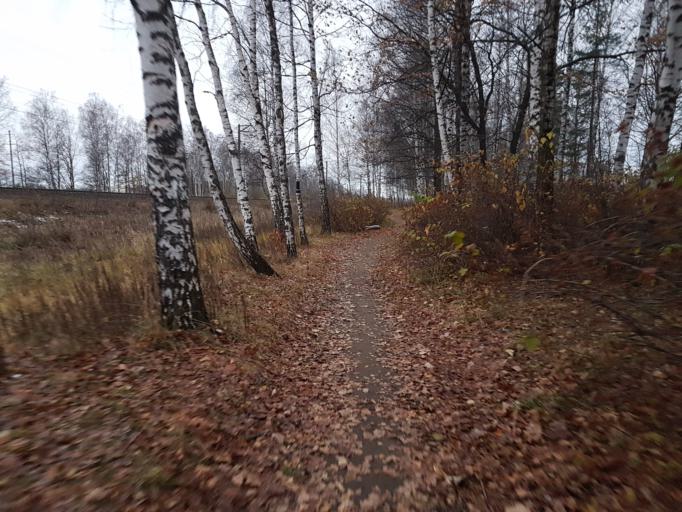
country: RU
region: Moskovskaya
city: Istra
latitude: 55.9021
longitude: 36.8739
